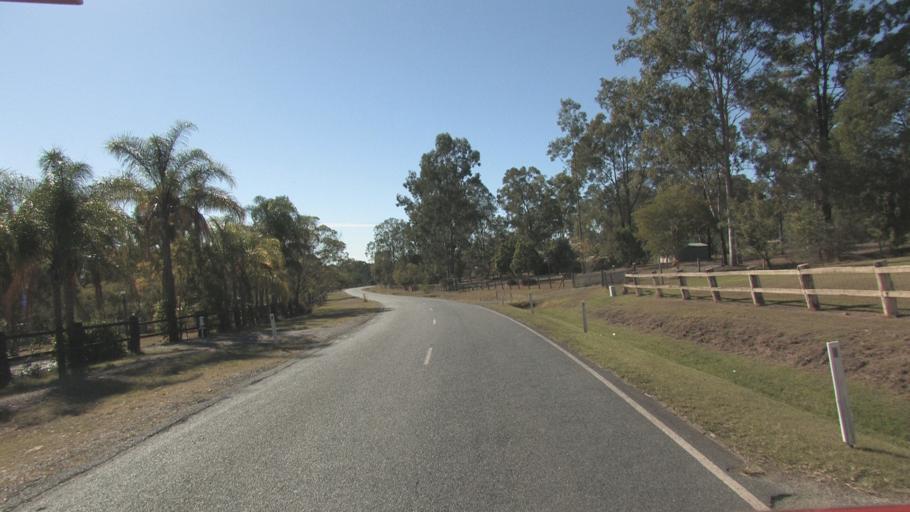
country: AU
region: Queensland
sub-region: Logan
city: North Maclean
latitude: -27.8262
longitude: 152.9467
